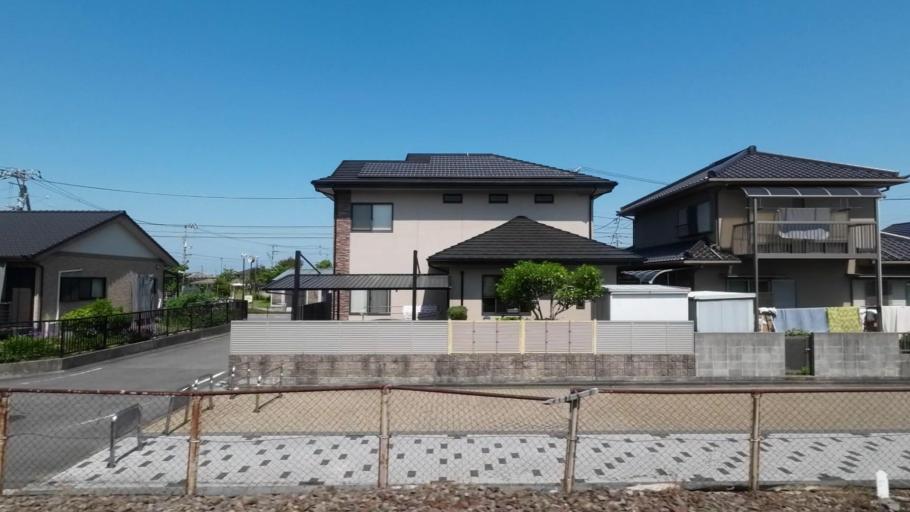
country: JP
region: Ehime
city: Niihama
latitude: 33.9499
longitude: 133.2967
